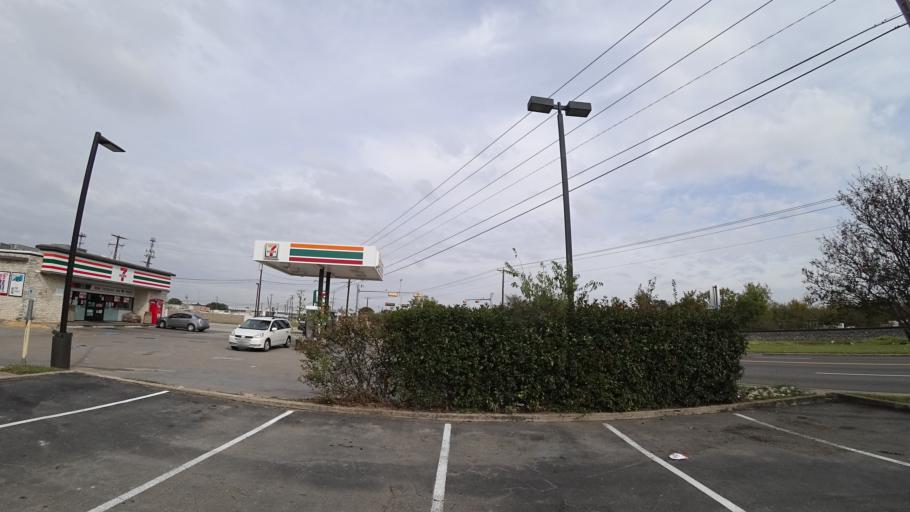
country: US
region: Texas
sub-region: Williamson County
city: Round Rock
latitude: 30.5000
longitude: -97.6859
